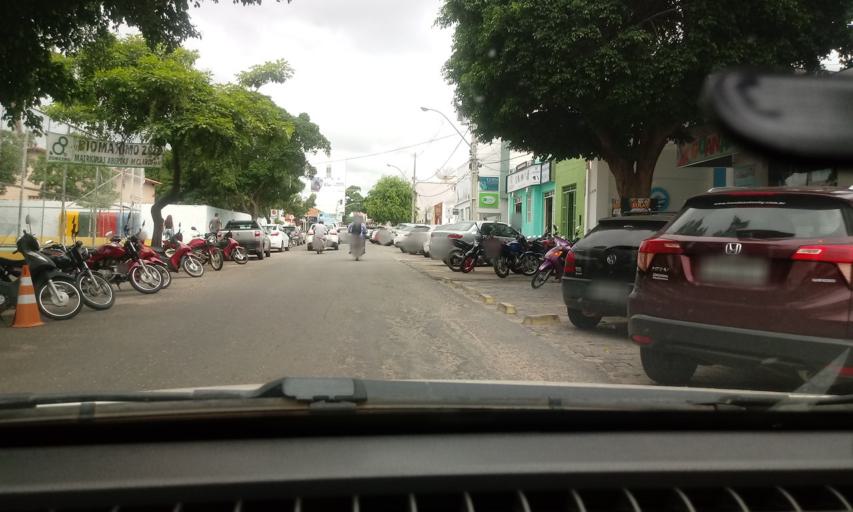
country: BR
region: Bahia
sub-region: Guanambi
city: Guanambi
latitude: -14.2223
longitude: -42.7790
